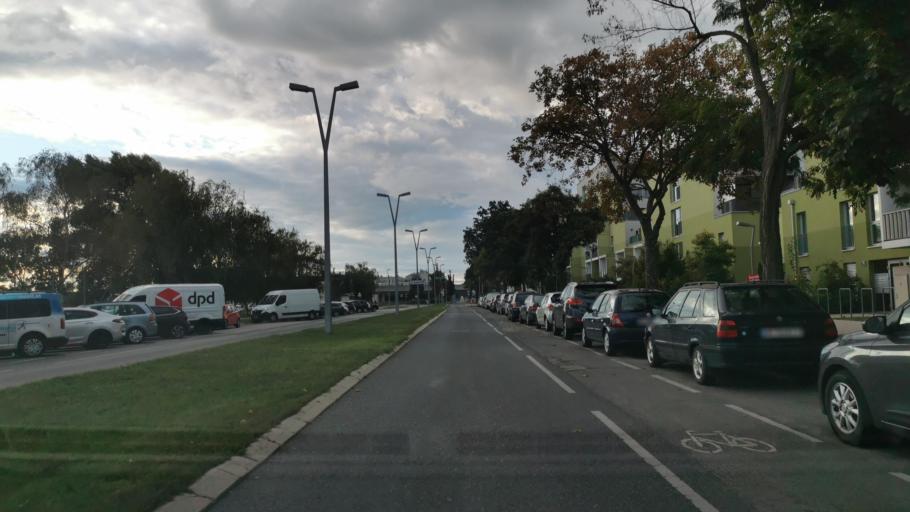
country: AT
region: Lower Austria
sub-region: Politischer Bezirk Wien-Umgebung
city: Gerasdorf bei Wien
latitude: 48.2265
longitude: 16.4736
